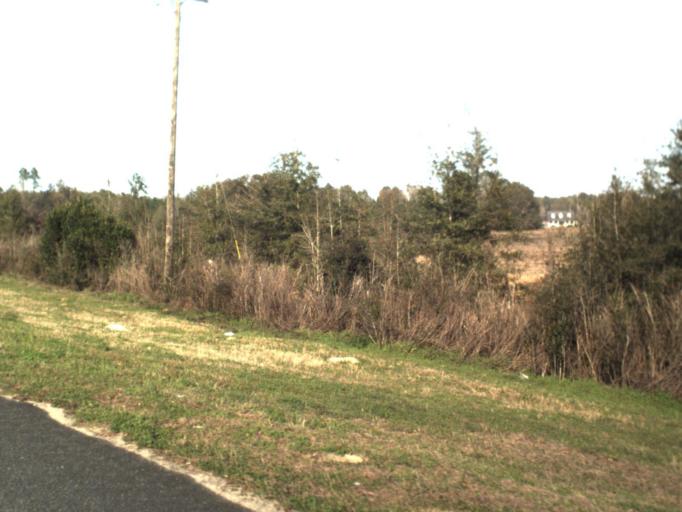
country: US
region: Florida
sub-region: Calhoun County
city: Blountstown
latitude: 30.5313
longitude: -85.1927
